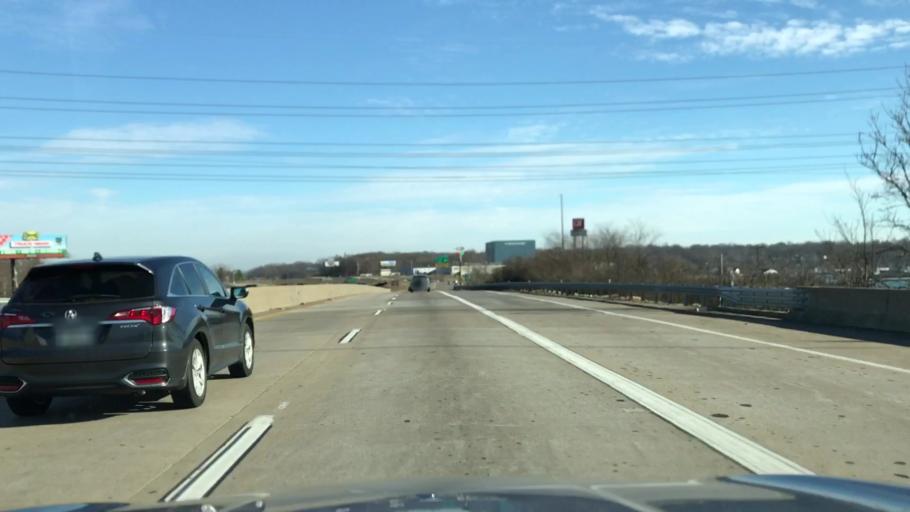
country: US
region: Missouri
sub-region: Saint Louis County
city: Glasgow Village
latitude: 38.7678
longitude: -90.2086
